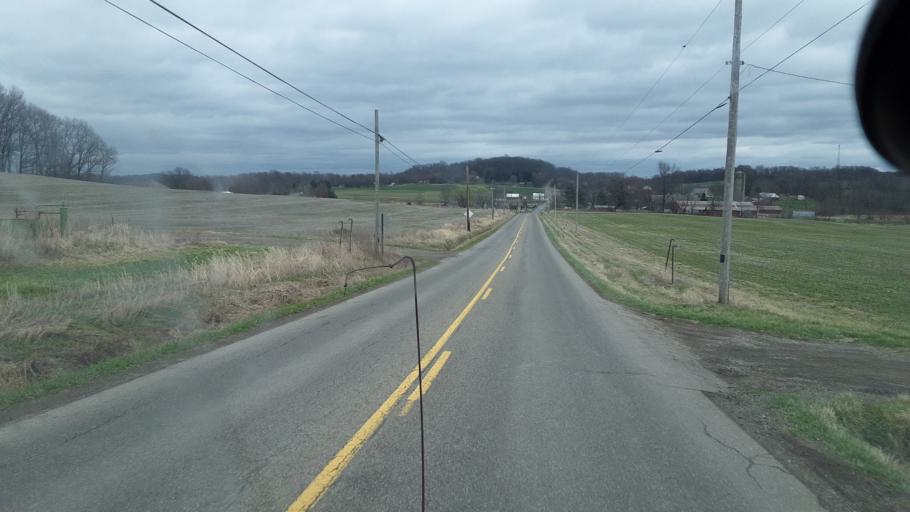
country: US
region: Ohio
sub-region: Stark County
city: Brewster
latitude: 40.7030
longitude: -81.6523
